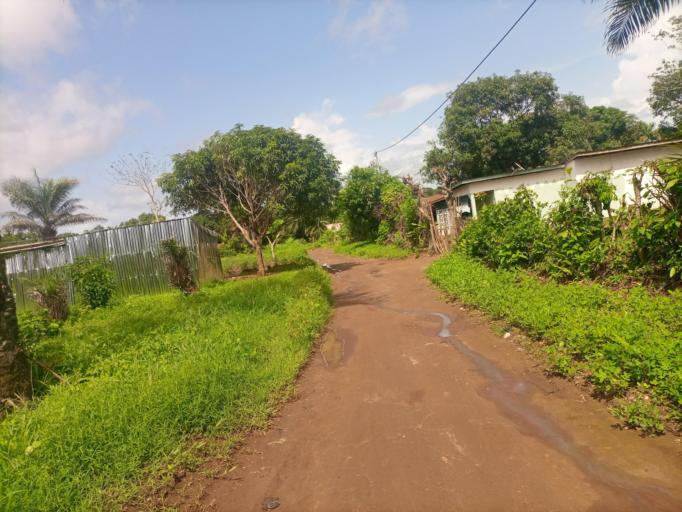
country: SL
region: Northern Province
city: Sawkta
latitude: 8.6339
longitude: -13.2105
